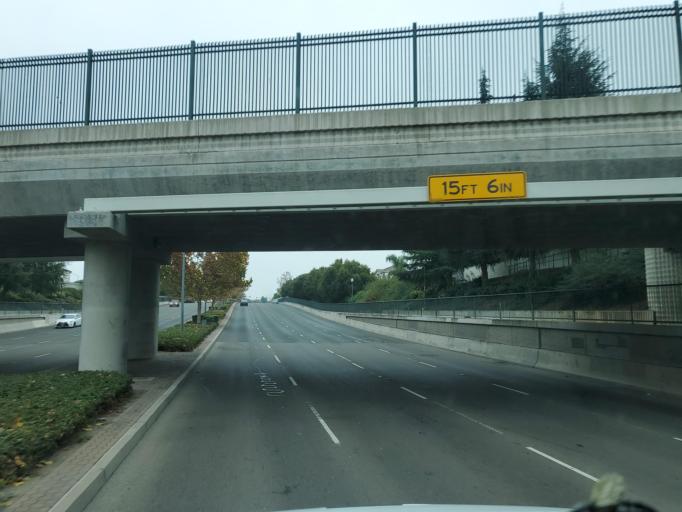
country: US
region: California
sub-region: San Joaquin County
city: August
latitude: 38.0045
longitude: -121.2811
